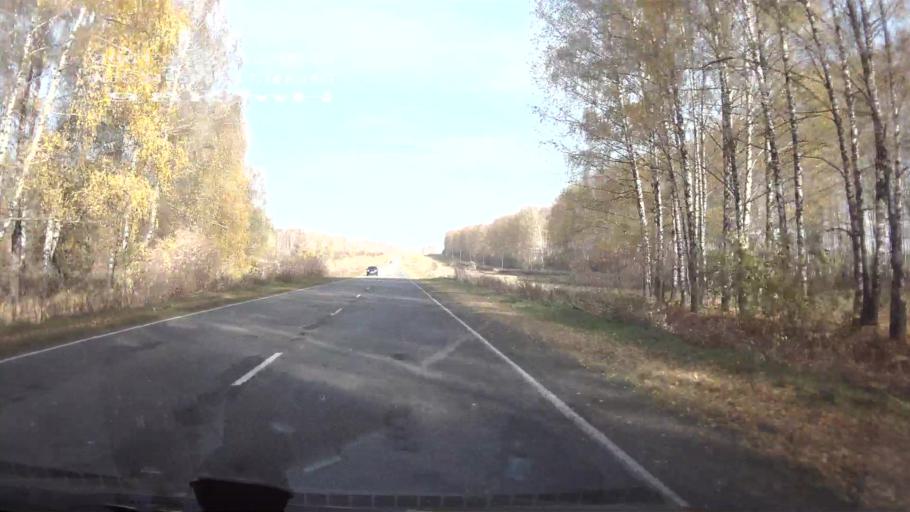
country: RU
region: Chuvashia
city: Ibresi
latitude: 55.3495
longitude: 47.1881
